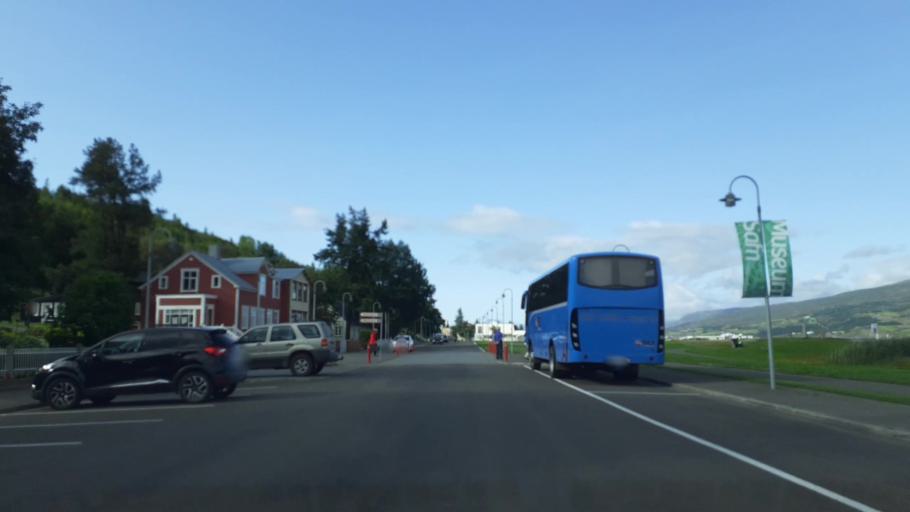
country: IS
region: Northeast
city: Akureyri
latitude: 65.6665
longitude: -18.0848
